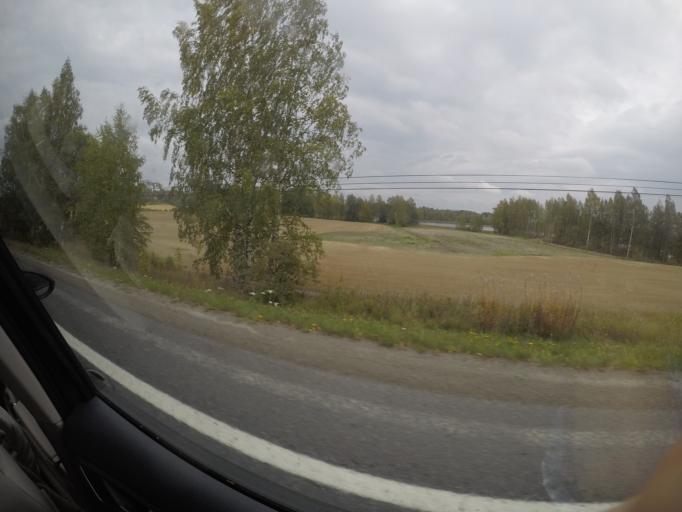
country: FI
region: Haeme
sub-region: Haemeenlinna
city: Parola
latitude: 61.0673
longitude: 24.3924
